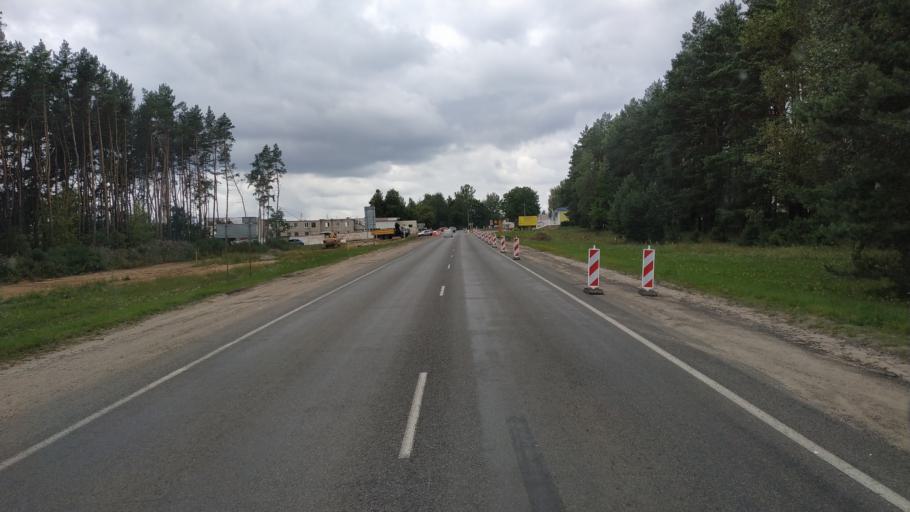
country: BY
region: Mogilev
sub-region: Mahilyowski Rayon
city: Veyno
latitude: 53.8789
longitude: 30.4129
